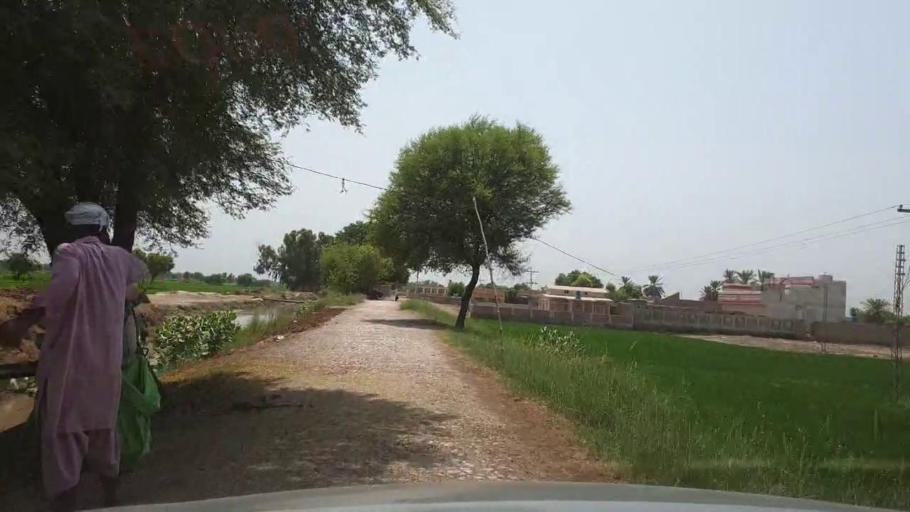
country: PK
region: Sindh
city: Ratodero
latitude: 27.7894
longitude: 68.3371
